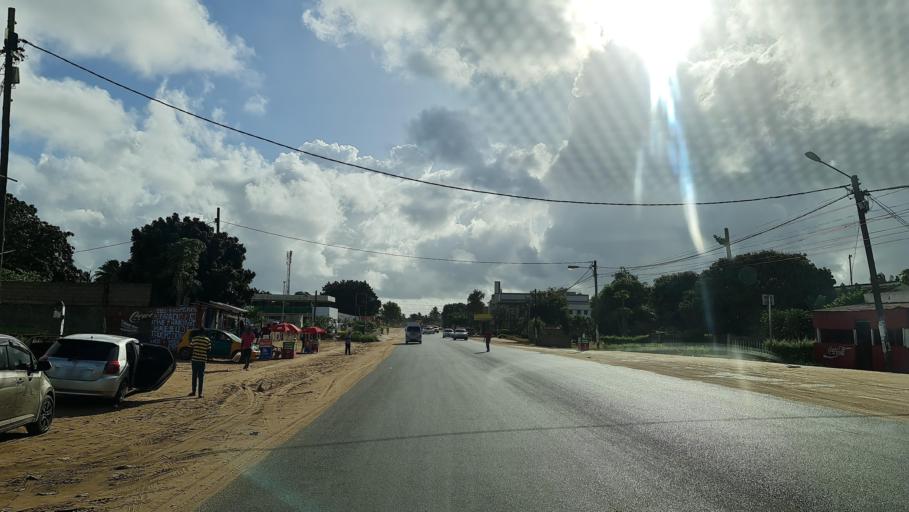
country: MZ
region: Gaza
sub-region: Xai-Xai District
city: Xai-Xai
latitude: -25.0567
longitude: 33.6643
